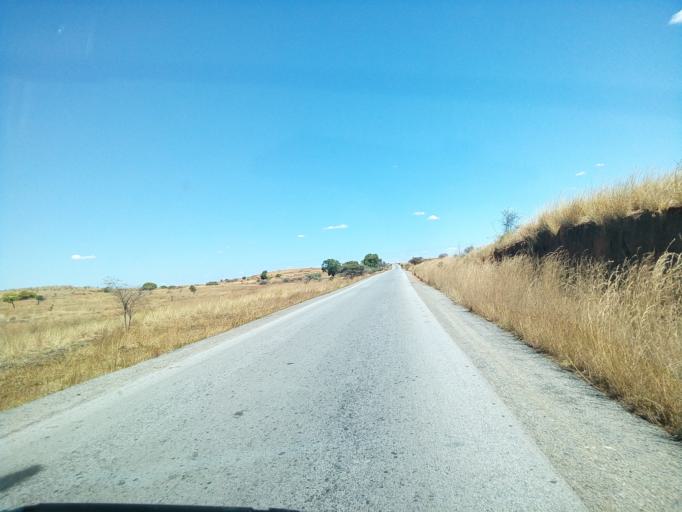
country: MG
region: Betsiboka
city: Maevatanana
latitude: -17.0981
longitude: 46.8134
